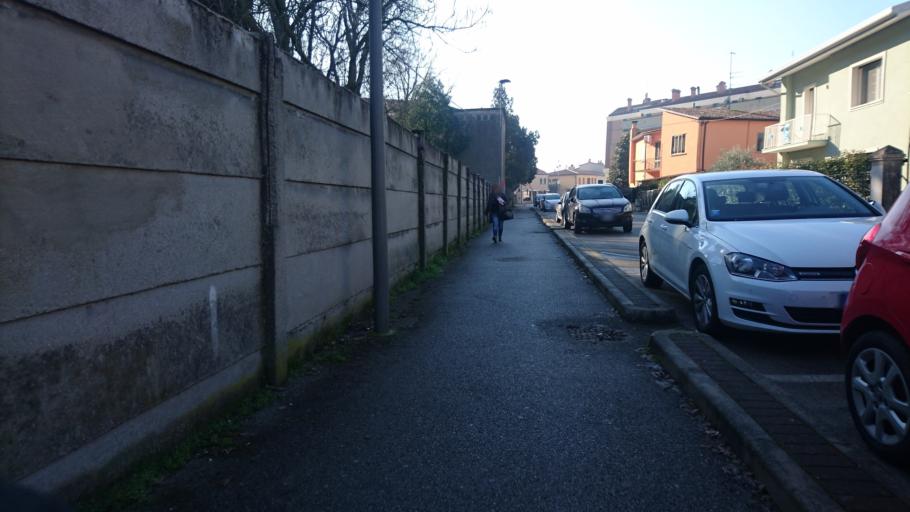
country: IT
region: Veneto
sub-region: Provincia di Padova
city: Conselve
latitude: 45.2344
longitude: 11.8708
